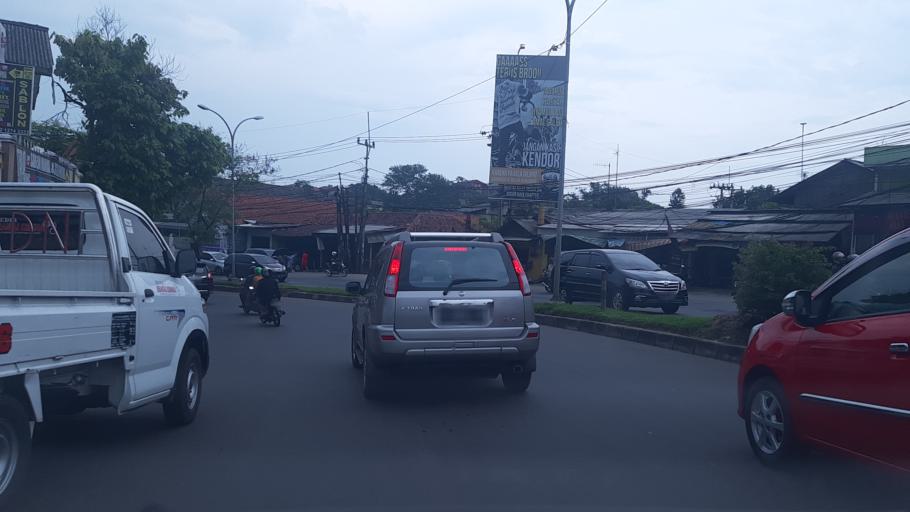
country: ID
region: West Java
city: Citeureup
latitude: -6.4806
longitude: 106.8686
